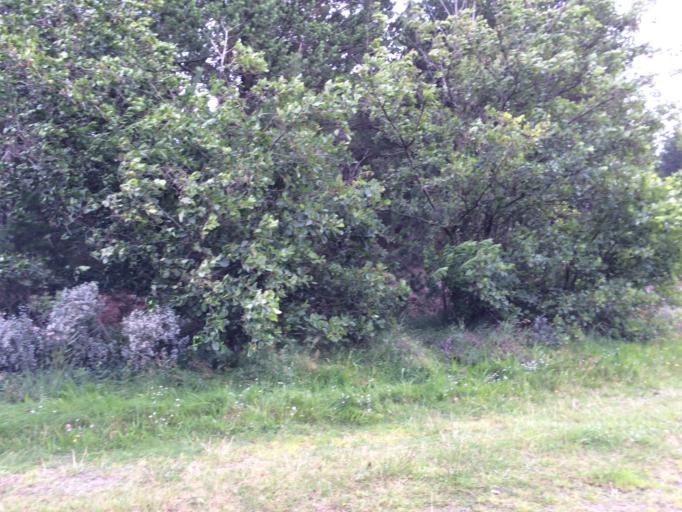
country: DK
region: Central Jutland
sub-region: Holstebro Kommune
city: Ulfborg
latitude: 56.2982
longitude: 8.1559
